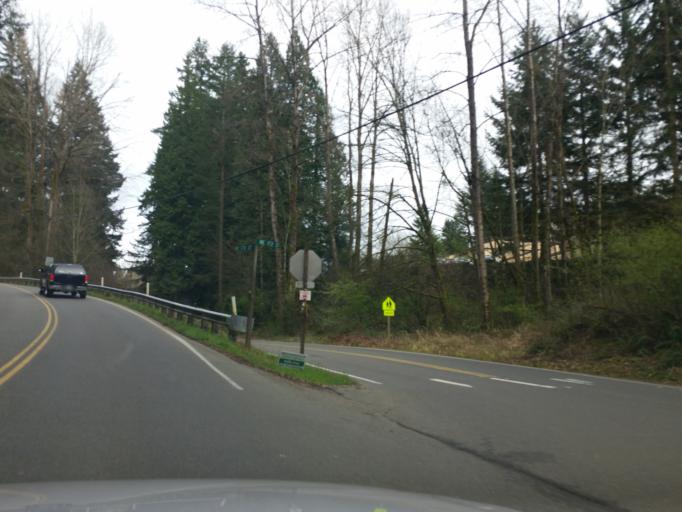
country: US
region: Washington
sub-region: King County
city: Woodinville
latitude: 47.7527
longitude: -122.1403
